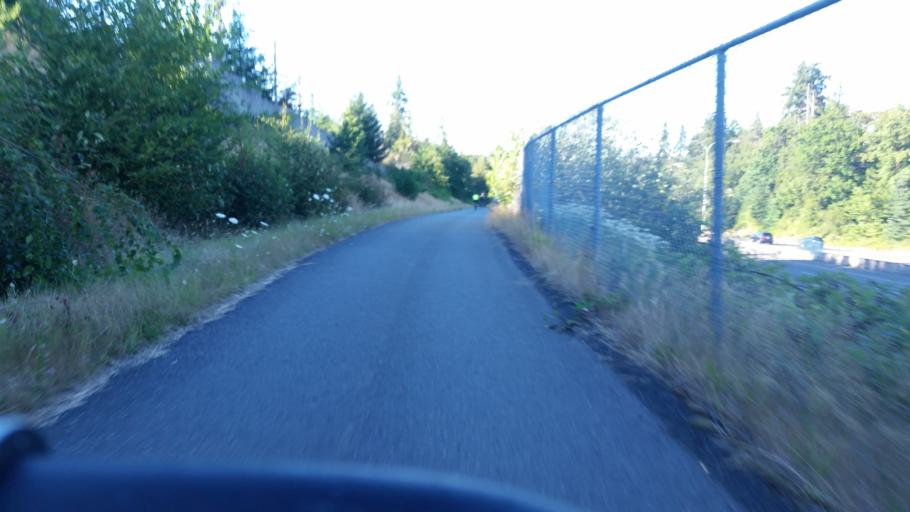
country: US
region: Washington
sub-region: King County
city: Redmond
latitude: 47.6612
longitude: -122.1354
